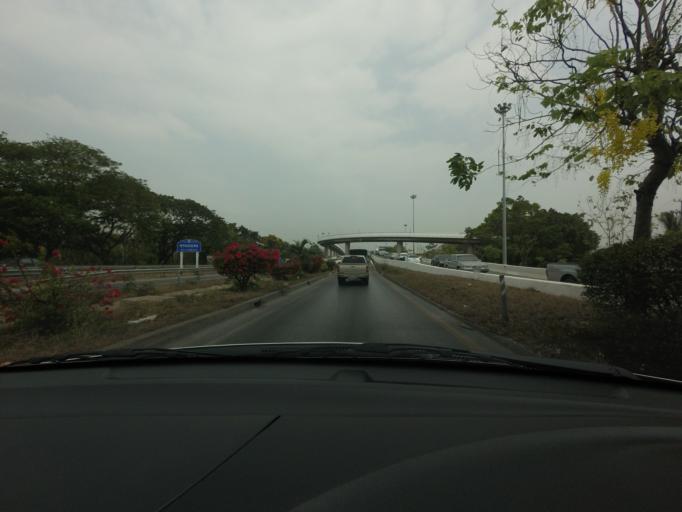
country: TH
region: Bangkok
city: Thawi Watthana
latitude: 13.7849
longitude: 100.3278
